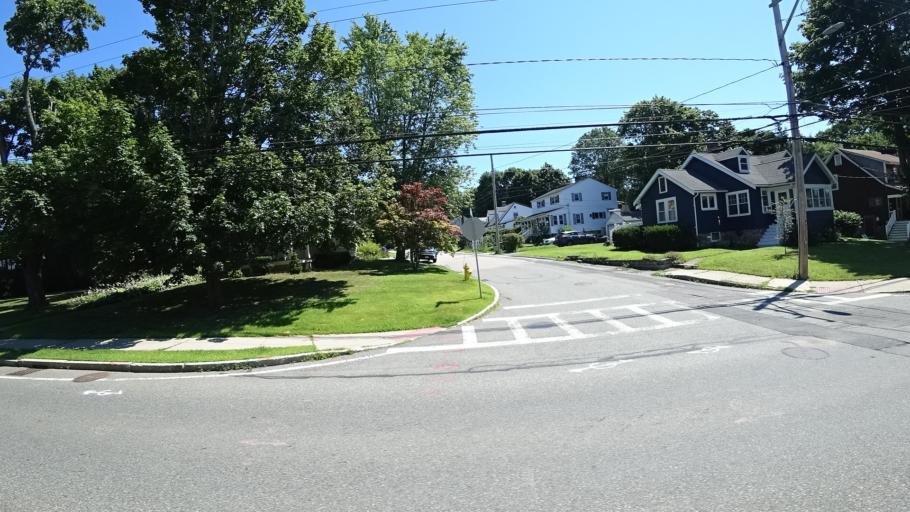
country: US
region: Massachusetts
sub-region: Norfolk County
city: Dedham
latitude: 42.2351
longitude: -71.1627
